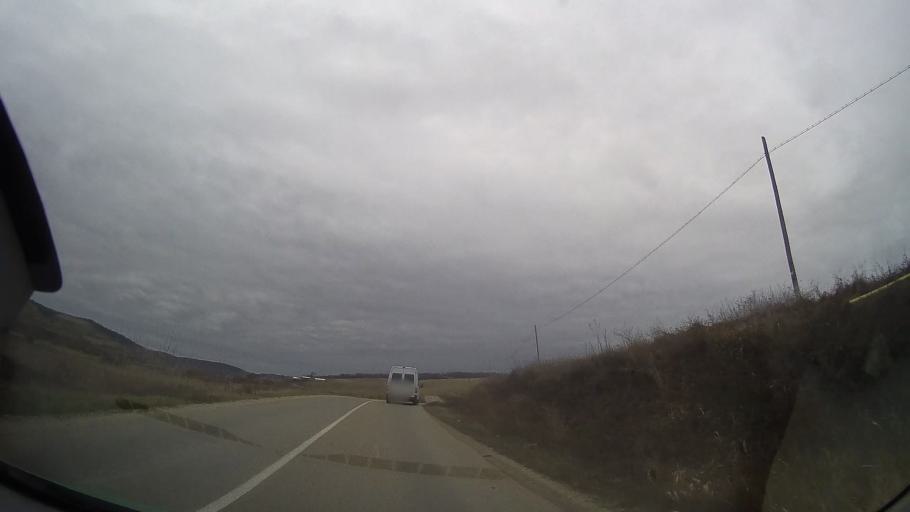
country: RO
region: Cluj
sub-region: Comuna Catina
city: Catina
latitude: 46.8070
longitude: 24.2172
